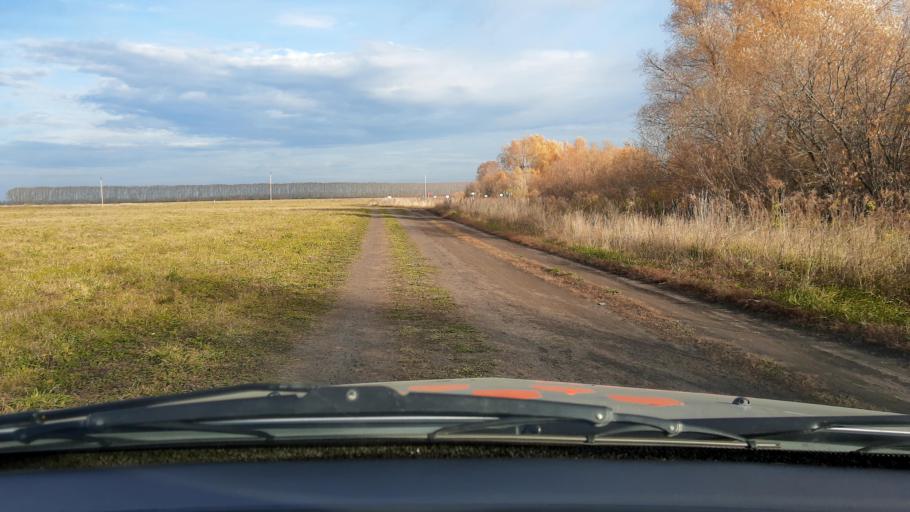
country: RU
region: Bashkortostan
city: Asanovo
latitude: 54.8071
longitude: 55.6117
